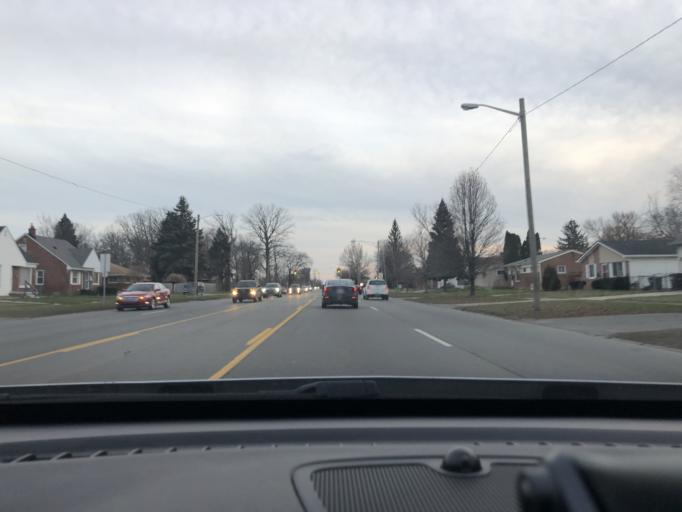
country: US
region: Michigan
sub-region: Wayne County
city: Allen Park
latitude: 42.2505
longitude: -83.2310
